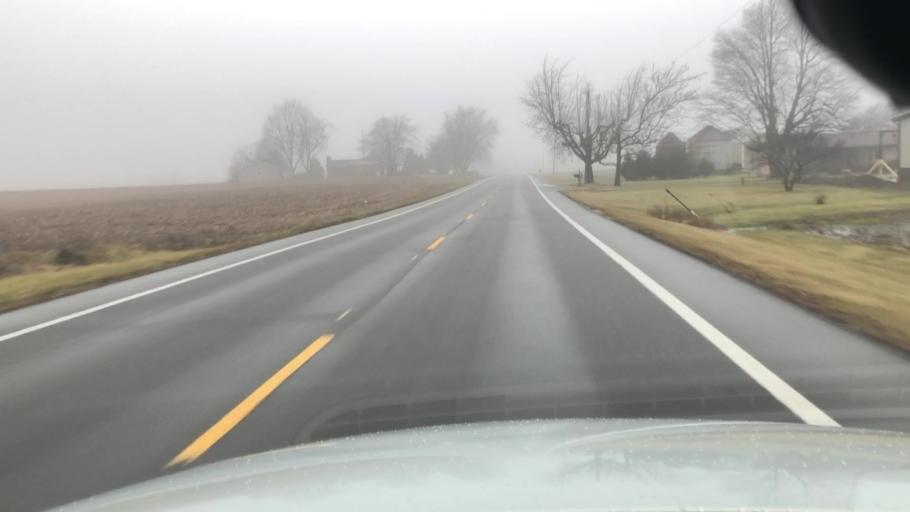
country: US
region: Ohio
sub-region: Logan County
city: Lakeview
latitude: 40.6035
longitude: -83.8820
